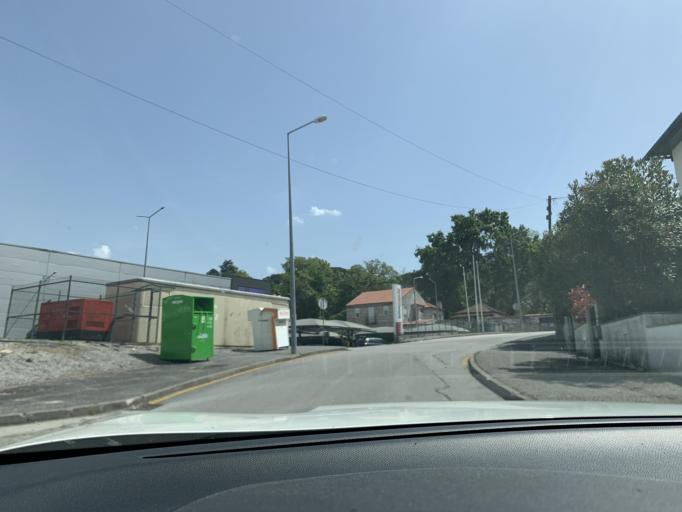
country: PT
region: Viseu
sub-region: Mangualde
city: Mangualde
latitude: 40.6050
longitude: -7.7689
